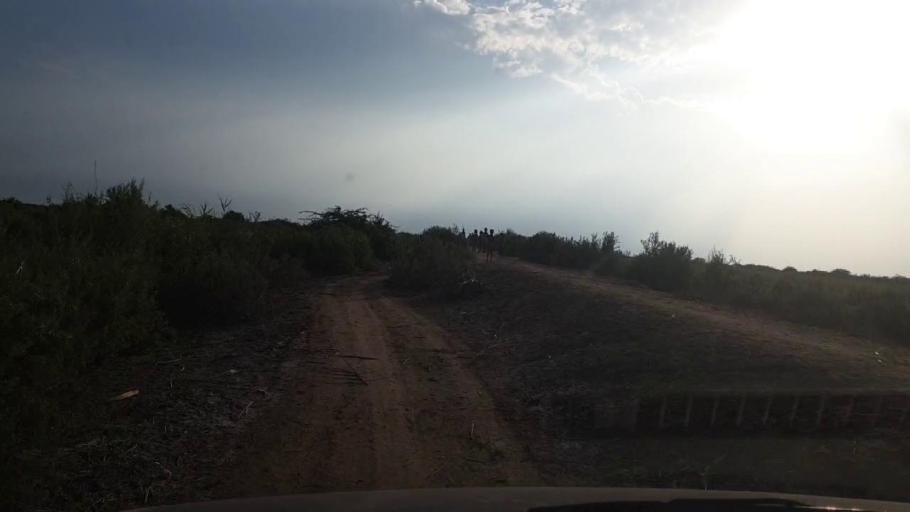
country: PK
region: Sindh
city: Badin
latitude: 24.4292
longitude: 68.6678
